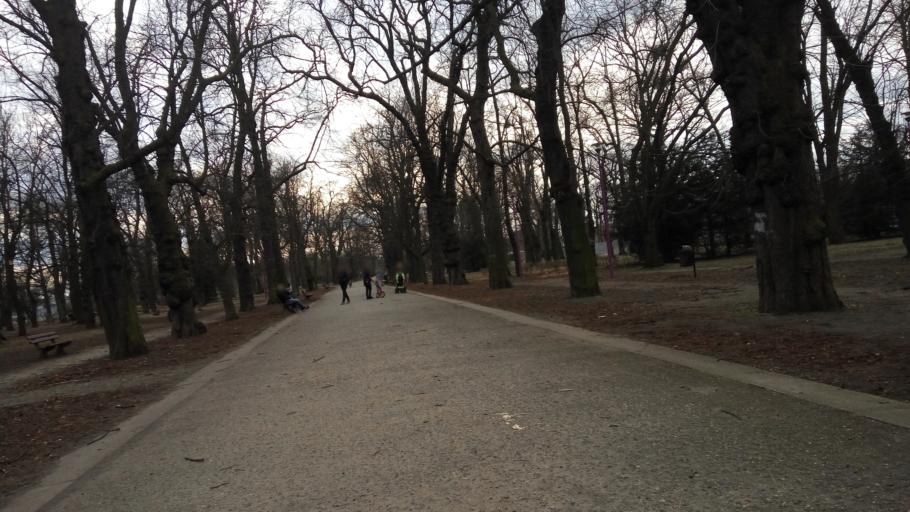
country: PL
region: Lower Silesian Voivodeship
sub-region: Powiat wroclawski
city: Wroclaw
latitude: 51.0878
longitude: 17.0301
